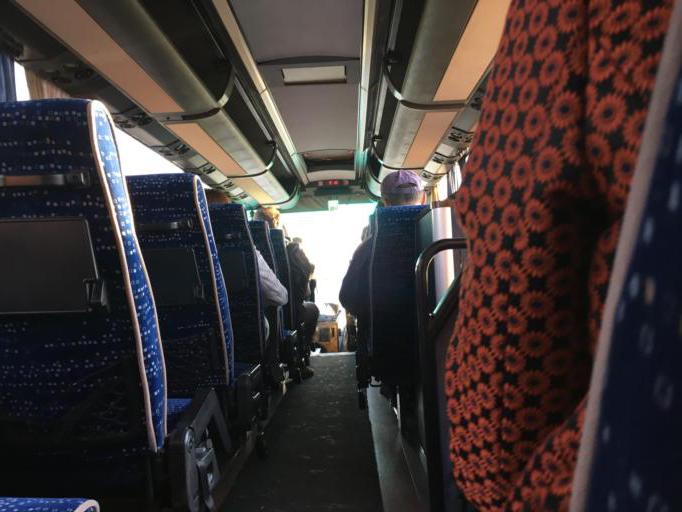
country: XK
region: Pristina
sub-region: Komuna e Drenasit
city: Glogovac
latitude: 42.6002
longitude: 20.8965
